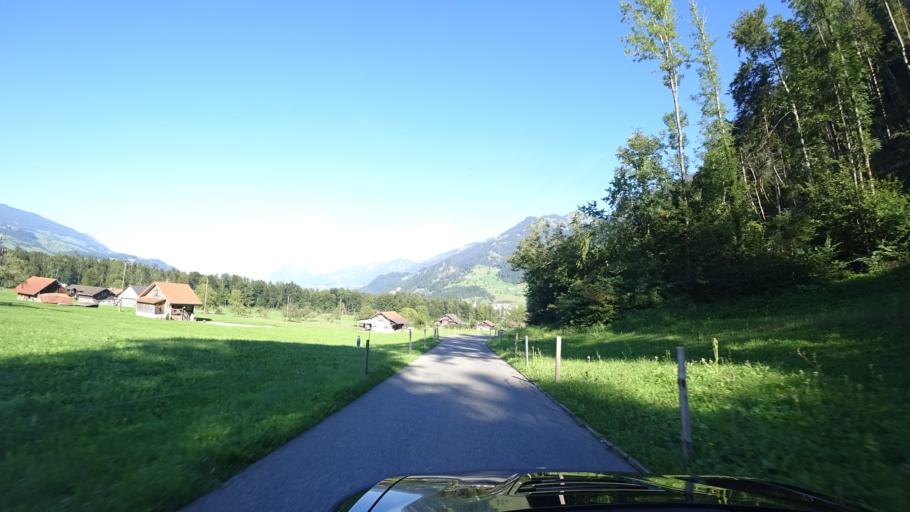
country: CH
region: Obwalden
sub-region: Obwalden
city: Giswil
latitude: 46.8292
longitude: 8.1601
